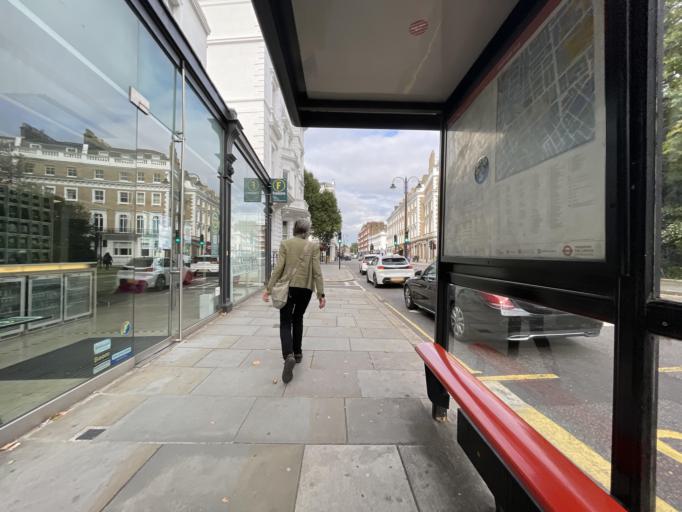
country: GB
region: England
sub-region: Greater London
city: Chelsea
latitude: 51.4919
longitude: -0.1789
